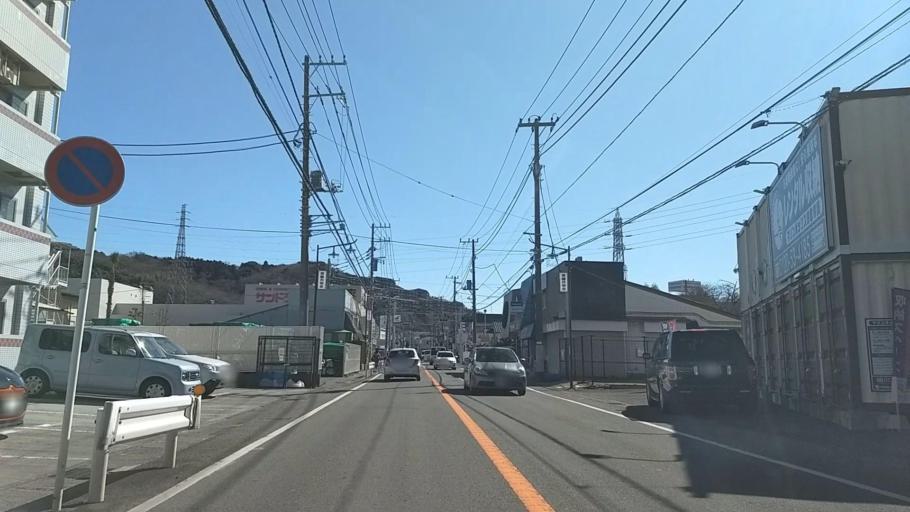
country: JP
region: Kanagawa
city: Kamakura
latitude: 35.3285
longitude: 139.5221
